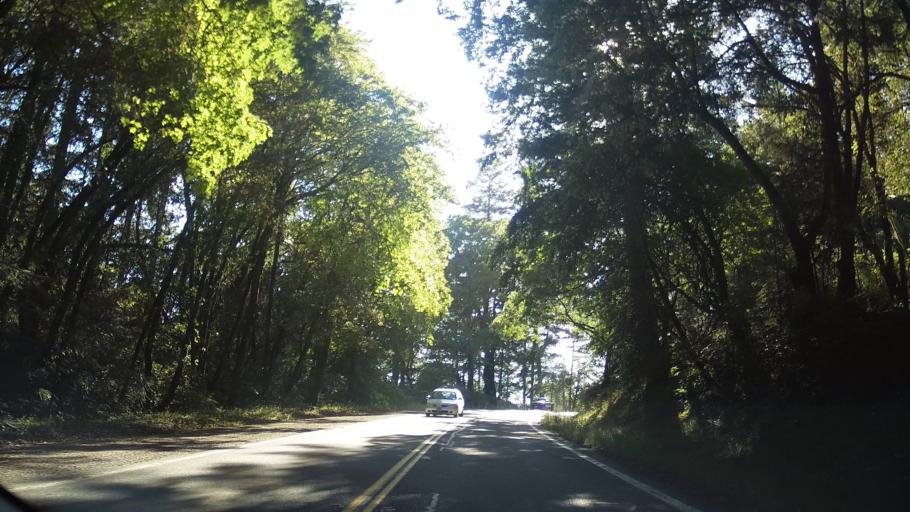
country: US
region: California
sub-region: Mendocino County
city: Brooktrails
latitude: 39.3884
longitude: -123.4411
